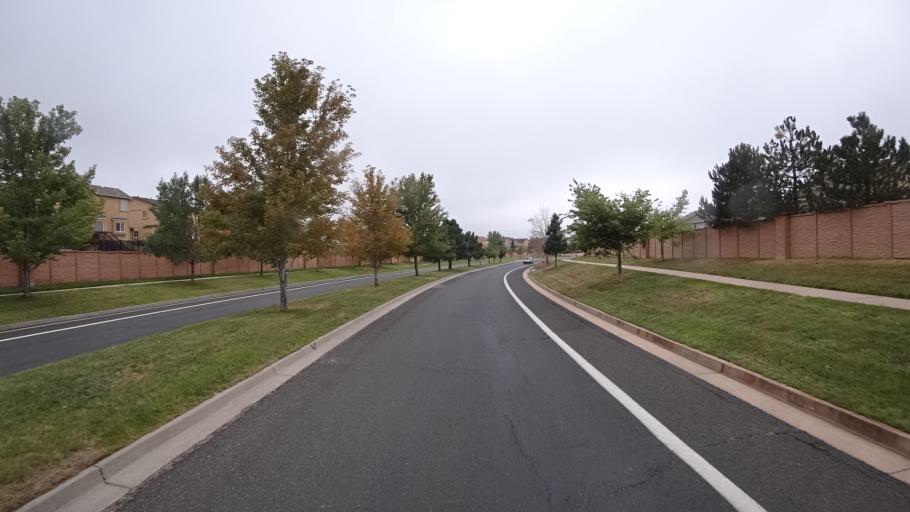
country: US
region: Colorado
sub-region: El Paso County
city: Cimarron Hills
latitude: 38.9337
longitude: -104.7232
